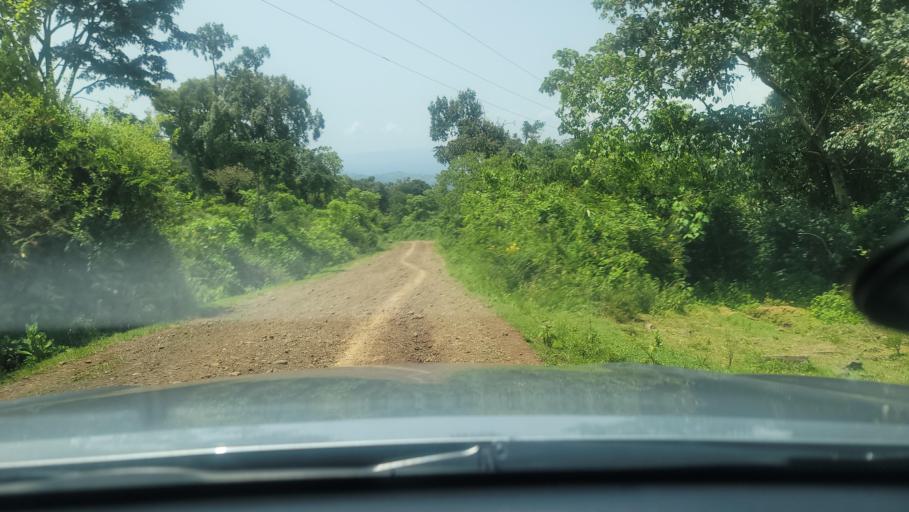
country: ET
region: Oromiya
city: Agaro
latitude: 7.8177
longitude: 36.4112
